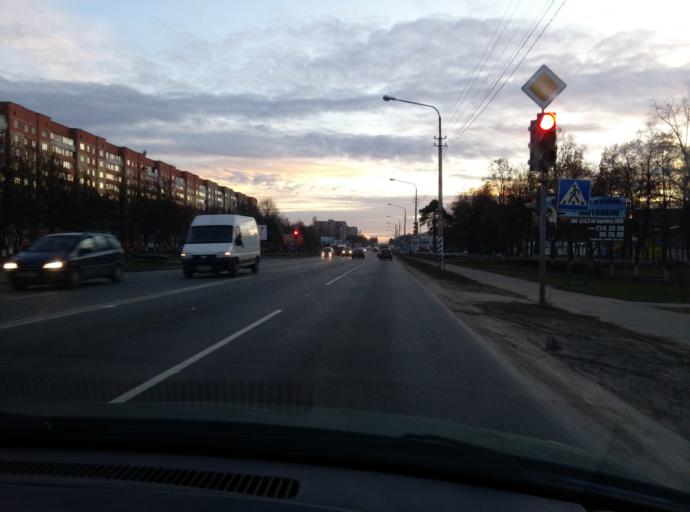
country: BY
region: Minsk
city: Horad Barysaw
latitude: 54.2236
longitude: 28.4935
